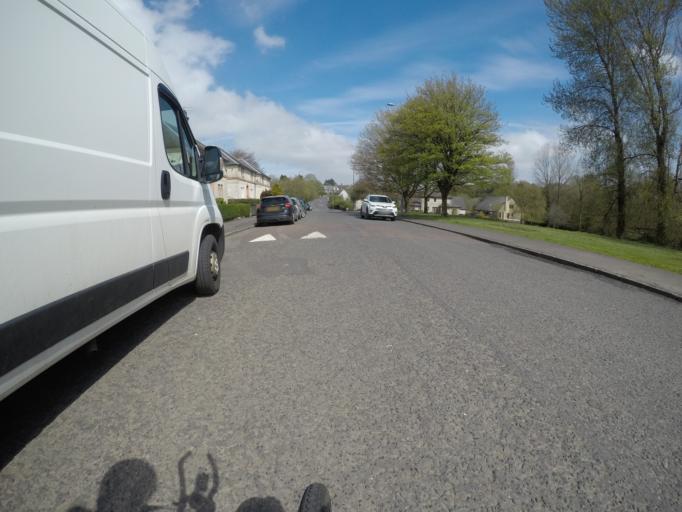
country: GB
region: Scotland
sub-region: East Ayrshire
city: Stewarton
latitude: 55.6845
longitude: -4.5078
